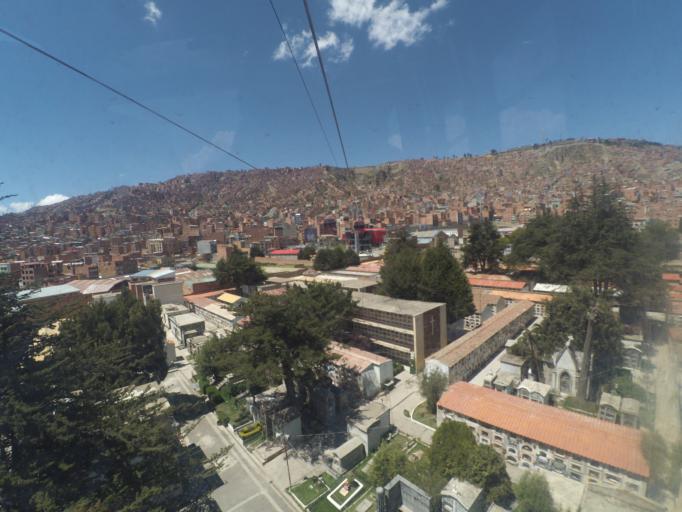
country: BO
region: La Paz
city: La Paz
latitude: -16.4966
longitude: -68.1510
